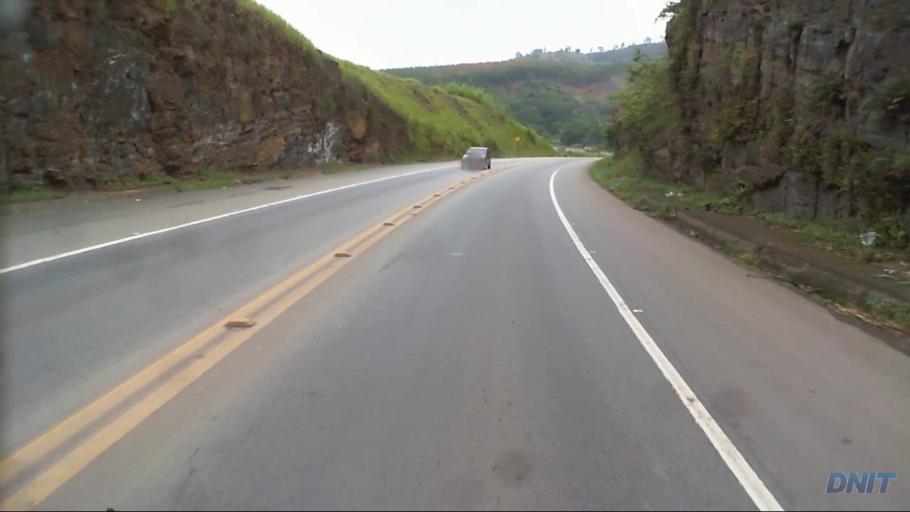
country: BR
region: Minas Gerais
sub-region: Coronel Fabriciano
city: Coronel Fabriciano
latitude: -19.5179
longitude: -42.5769
